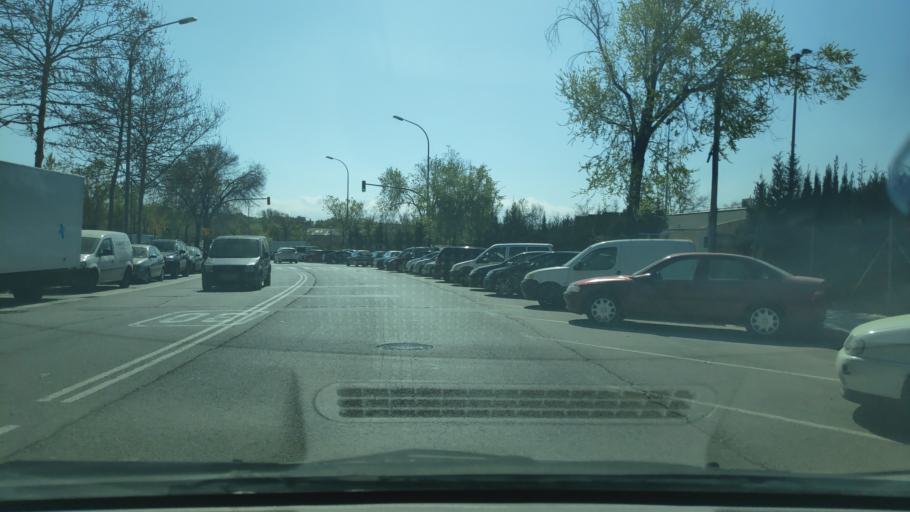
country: ES
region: Catalonia
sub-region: Provincia de Barcelona
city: Sabadell
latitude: 41.5457
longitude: 2.1286
